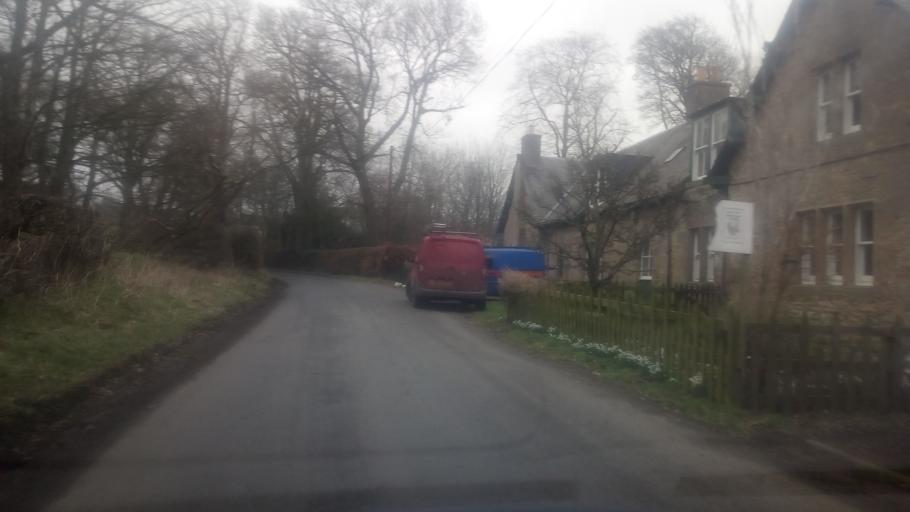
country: GB
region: Scotland
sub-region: The Scottish Borders
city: Jedburgh
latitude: 55.5255
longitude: -2.5165
